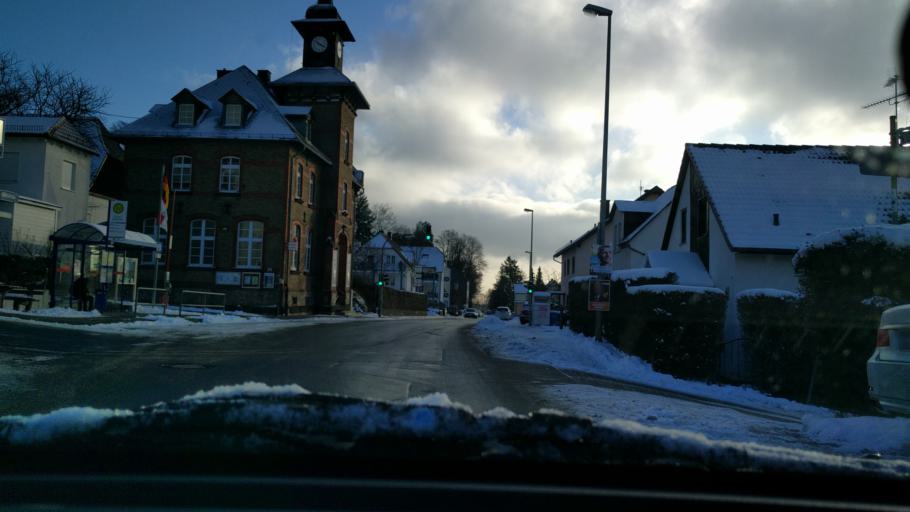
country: DE
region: Hesse
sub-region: Regierungsbezirk Darmstadt
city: Schlangenbad
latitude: 50.0886
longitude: 8.1203
